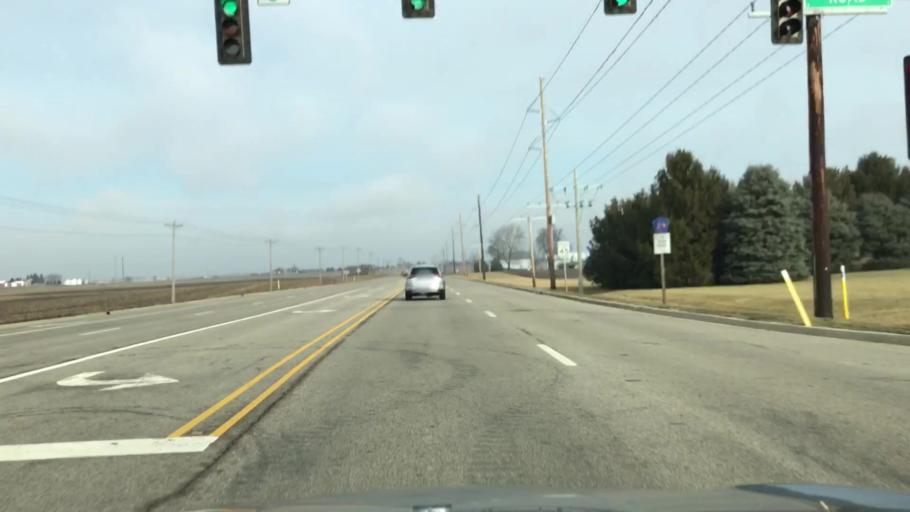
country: US
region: Illinois
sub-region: McLean County
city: Normal
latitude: 40.5175
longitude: -88.9029
